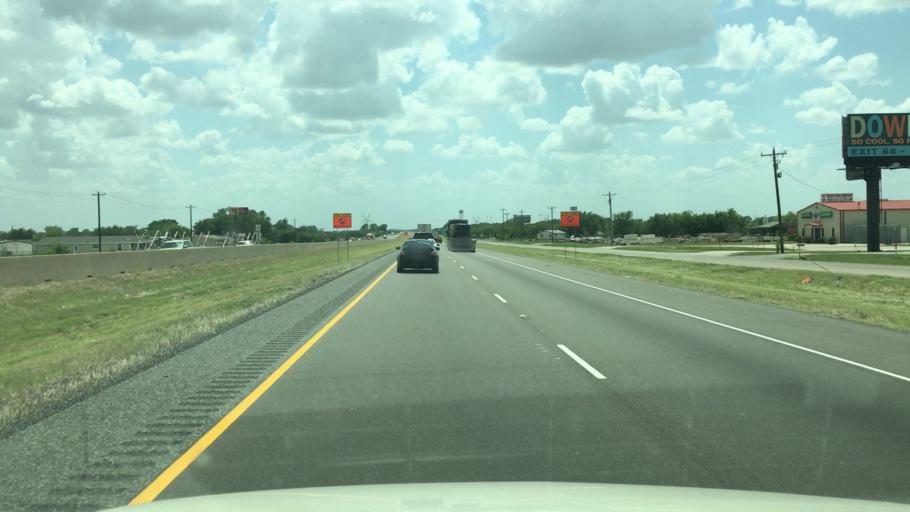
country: US
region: Texas
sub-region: Hunt County
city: Caddo Mills
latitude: 33.0048
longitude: -96.2298
